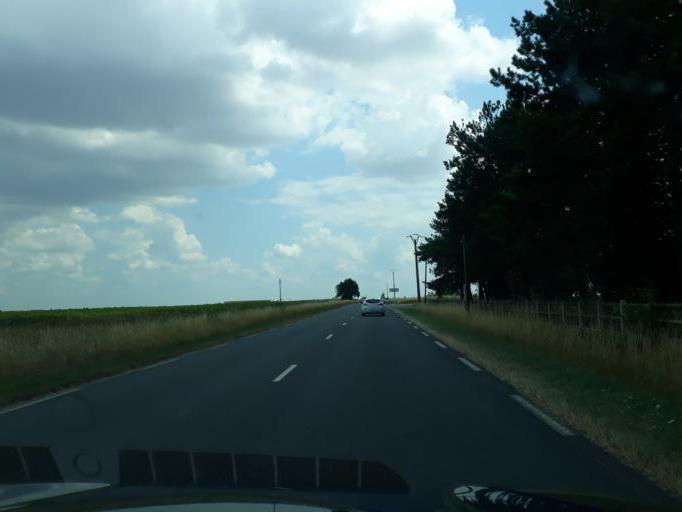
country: FR
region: Centre
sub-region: Departement du Cher
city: Avord
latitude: 47.0336
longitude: 2.6316
